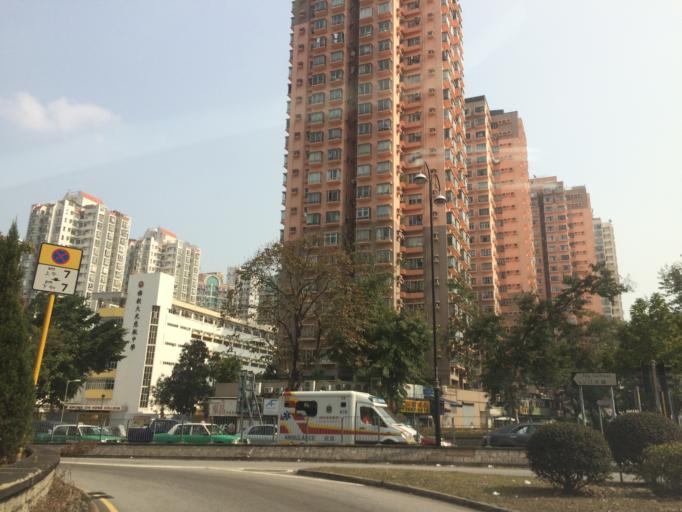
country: HK
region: Tai Po
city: Tai Po
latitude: 22.4530
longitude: 114.1619
